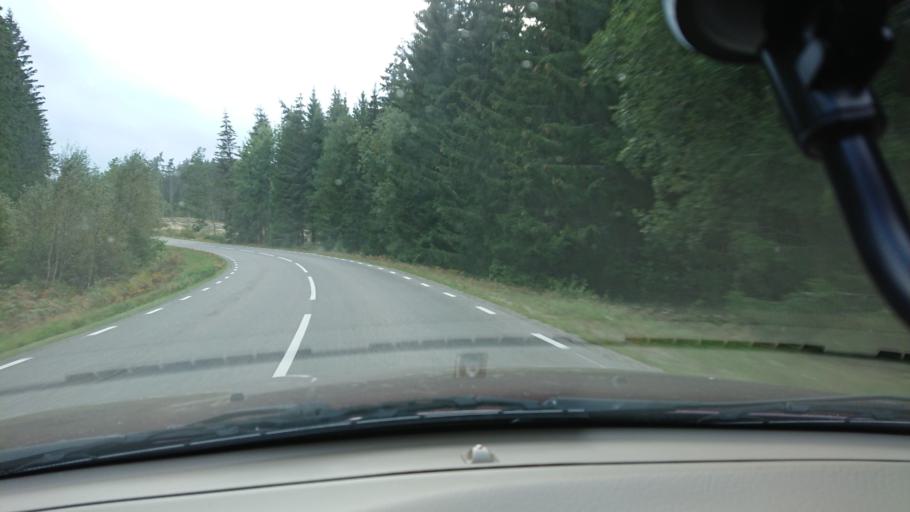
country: SE
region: Kronoberg
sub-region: Vaxjo Kommun
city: Lammhult
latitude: 57.0971
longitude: 14.6799
